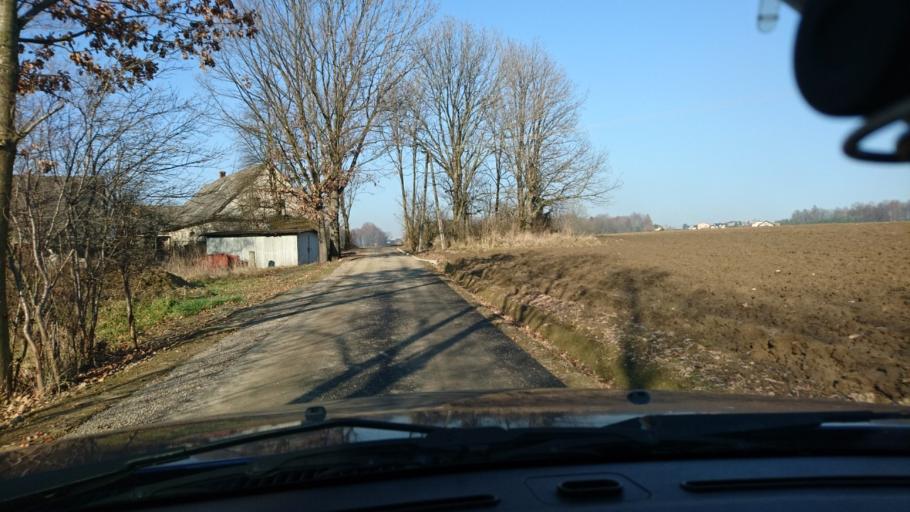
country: PL
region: Silesian Voivodeship
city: Janowice
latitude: 49.8952
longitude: 19.0794
